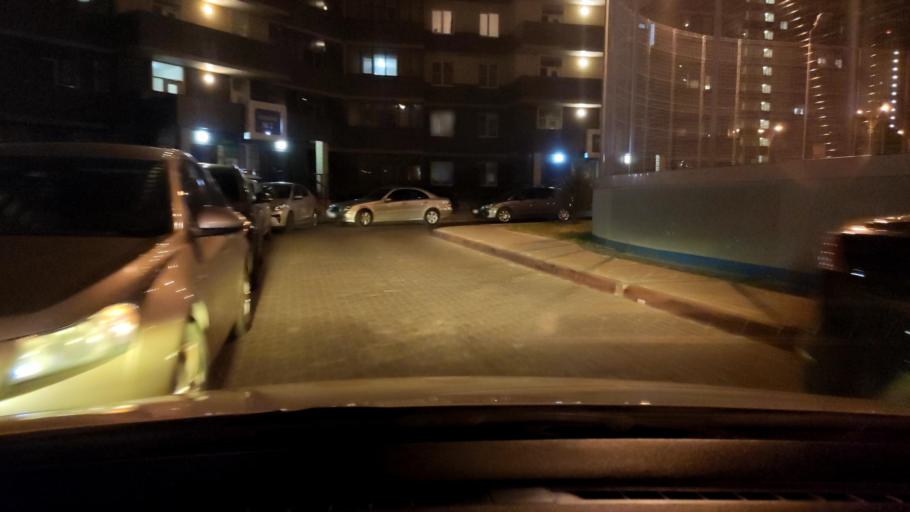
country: RU
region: Voronezj
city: Voronezh
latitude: 51.7160
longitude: 39.1981
